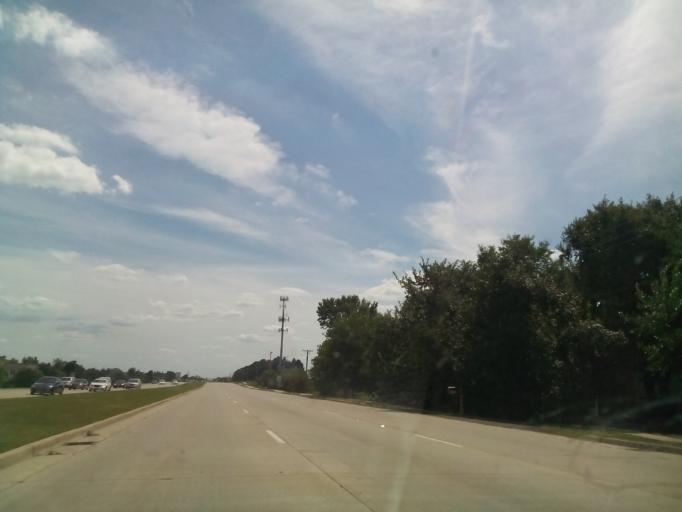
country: US
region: Illinois
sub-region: DuPage County
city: Naperville
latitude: 41.7230
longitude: -88.2062
